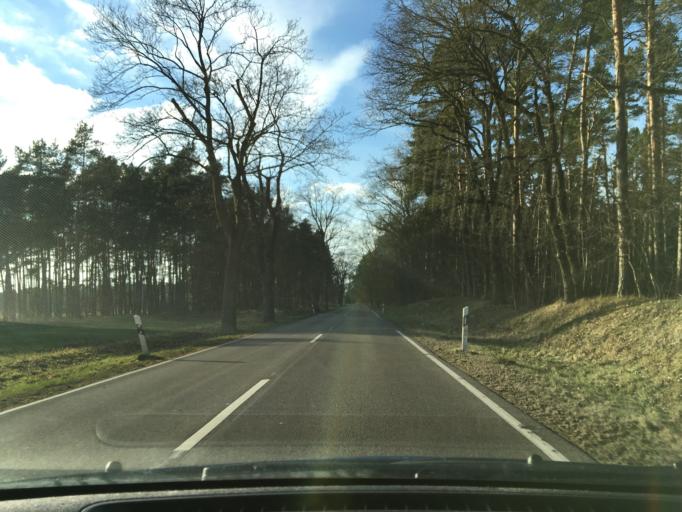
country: DE
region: Saxony-Anhalt
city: Luftkurort Arendsee
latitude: 52.8848
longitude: 11.5947
